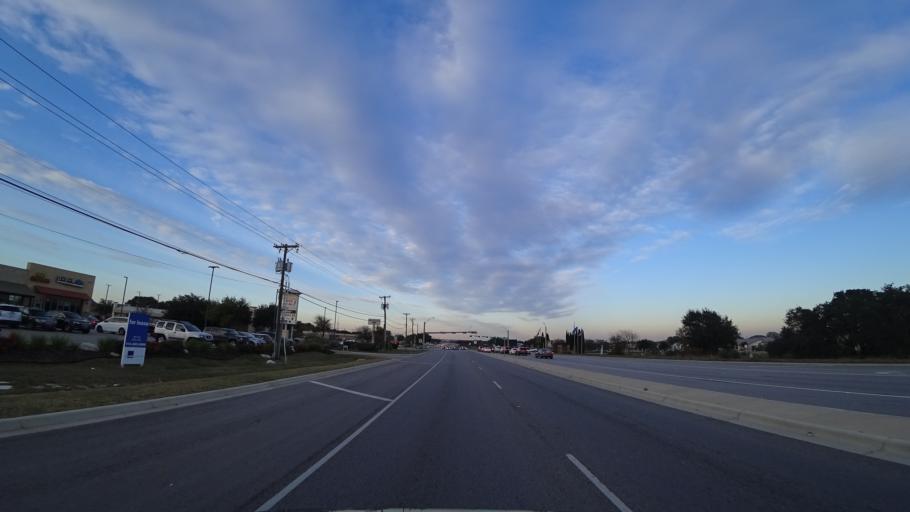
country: US
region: Texas
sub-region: Williamson County
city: Brushy Creek
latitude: 30.4926
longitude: -97.7264
